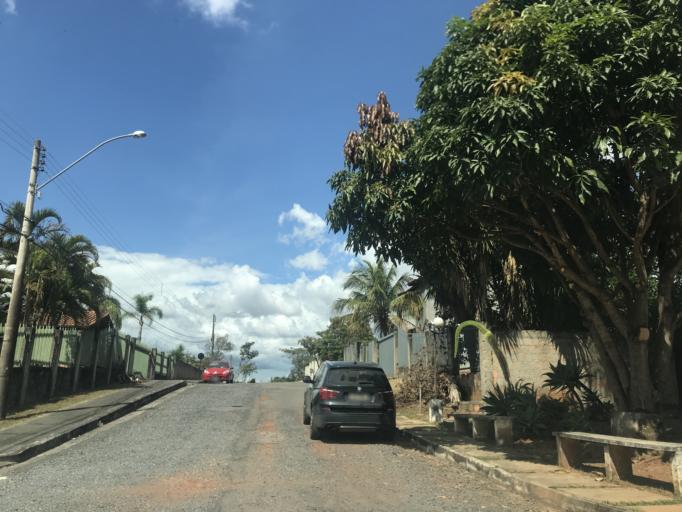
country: BR
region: Federal District
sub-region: Brasilia
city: Brasilia
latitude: -15.8651
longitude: -47.7540
